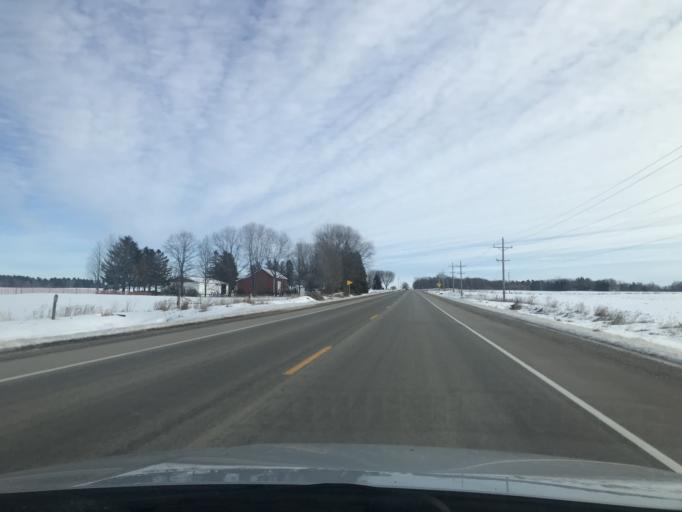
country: US
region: Wisconsin
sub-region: Oconto County
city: Oconto Falls
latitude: 44.8946
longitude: -88.1796
